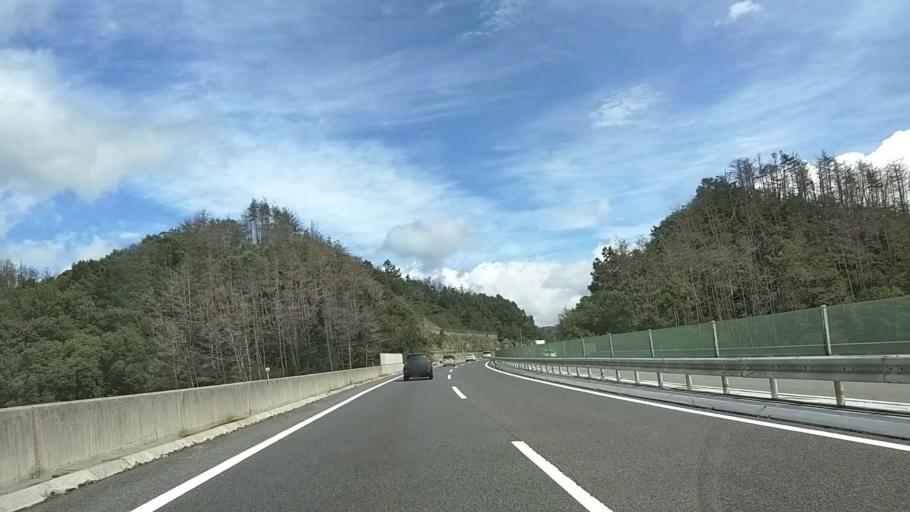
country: JP
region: Nagano
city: Hotaka
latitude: 36.4328
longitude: 138.0116
